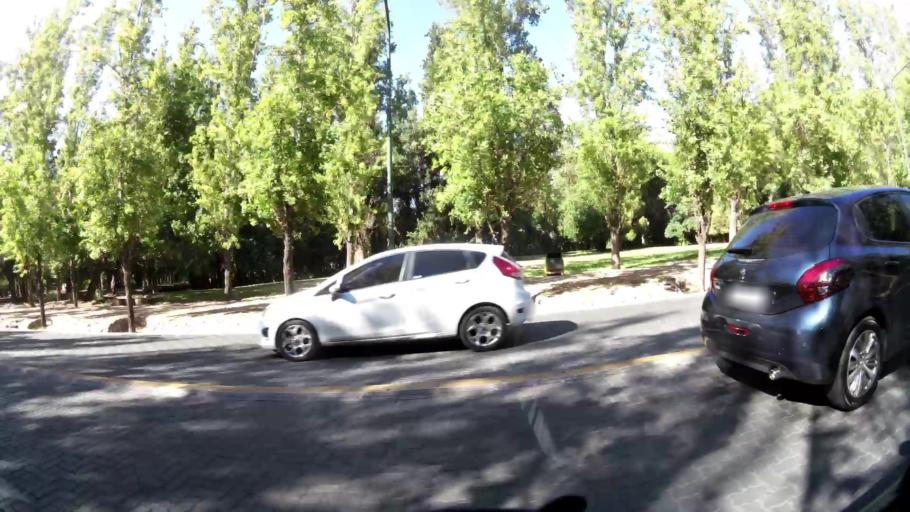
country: AR
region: Mendoza
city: Mendoza
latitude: -32.8860
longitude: -68.8645
